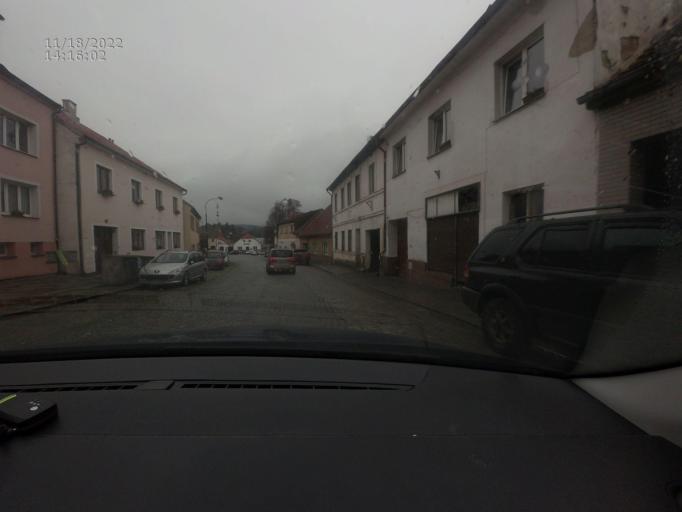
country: CZ
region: Jihocesky
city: Mirotice
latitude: 49.4292
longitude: 14.0371
